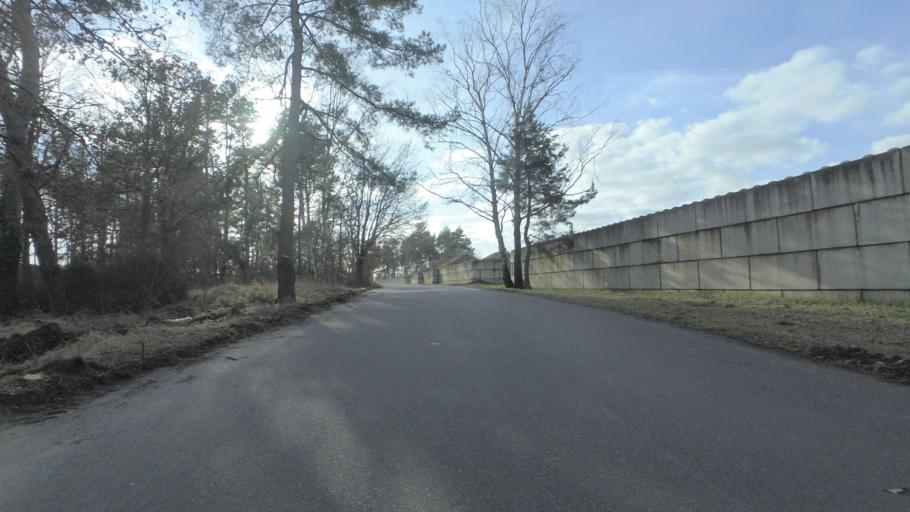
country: DE
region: Brandenburg
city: Trebbin
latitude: 52.2234
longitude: 13.2382
